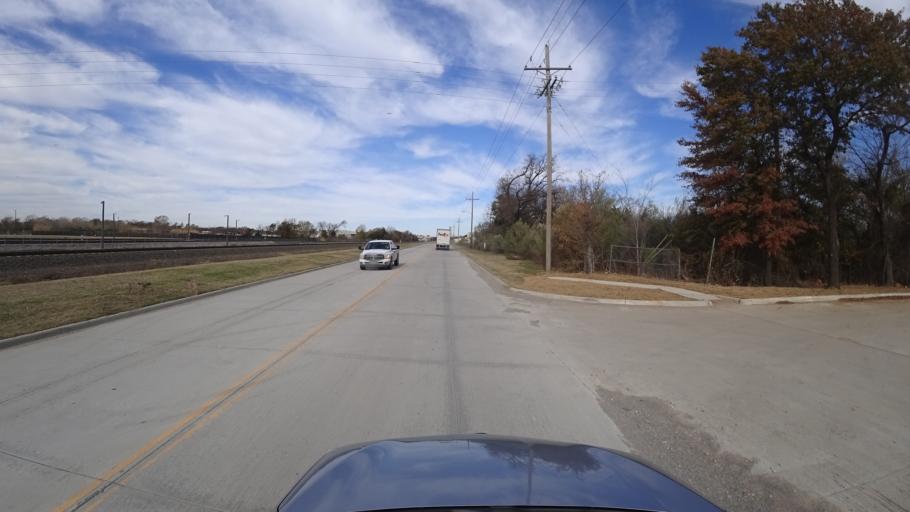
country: US
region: Texas
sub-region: Denton County
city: Lewisville
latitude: 33.0368
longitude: -96.9804
